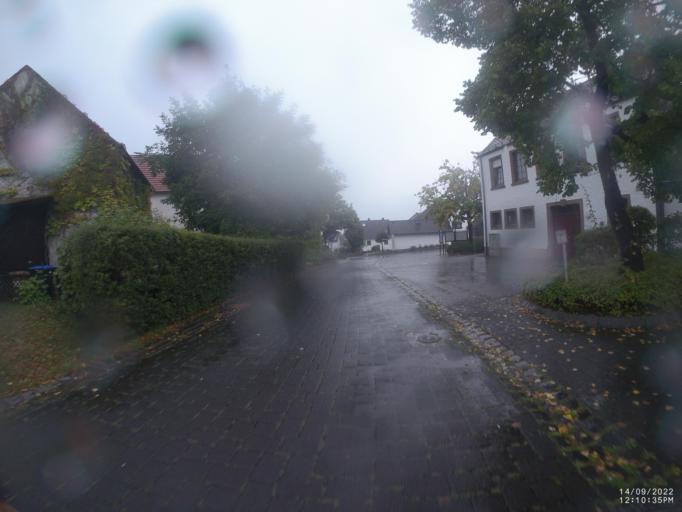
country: DE
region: Rheinland-Pfalz
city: Uxheim
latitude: 50.3424
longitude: 6.7428
